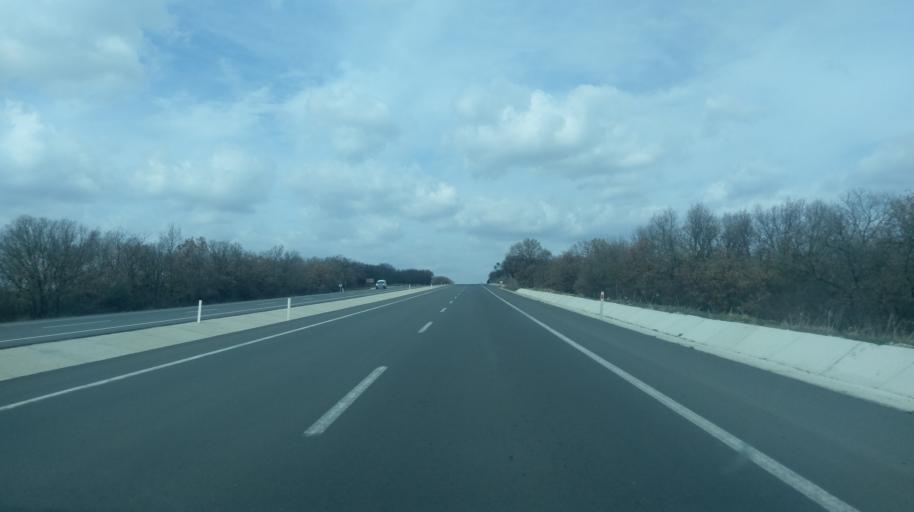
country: TR
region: Edirne
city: Kesan
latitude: 40.8938
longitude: 26.6341
